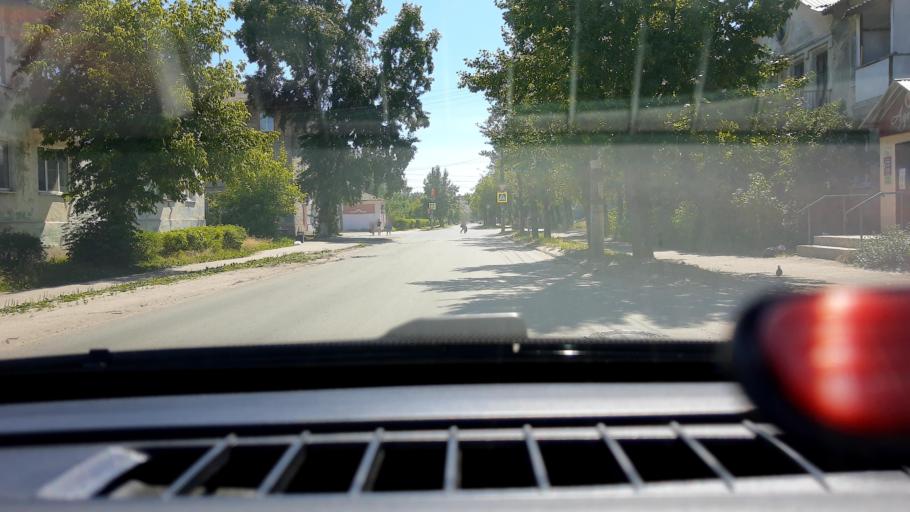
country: RU
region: Nizjnij Novgorod
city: Dzerzhinsk
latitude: 56.2483
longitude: 43.4728
